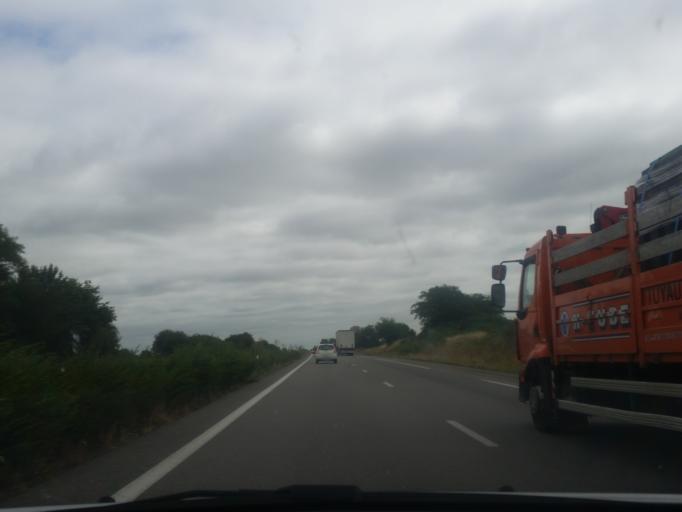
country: FR
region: Pays de la Loire
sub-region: Departement de la Loire-Atlantique
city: Le Cellier
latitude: 47.3581
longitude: -1.3267
